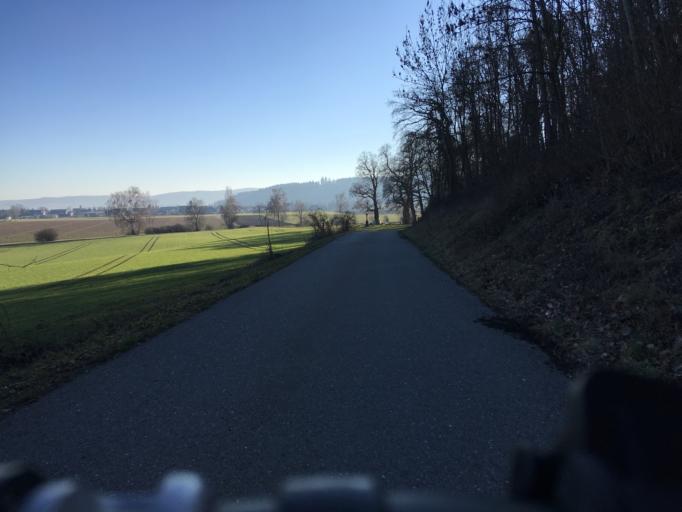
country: CH
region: Schaffhausen
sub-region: Bezirk Stein
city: Ramsen
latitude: 47.7180
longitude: 8.8085
